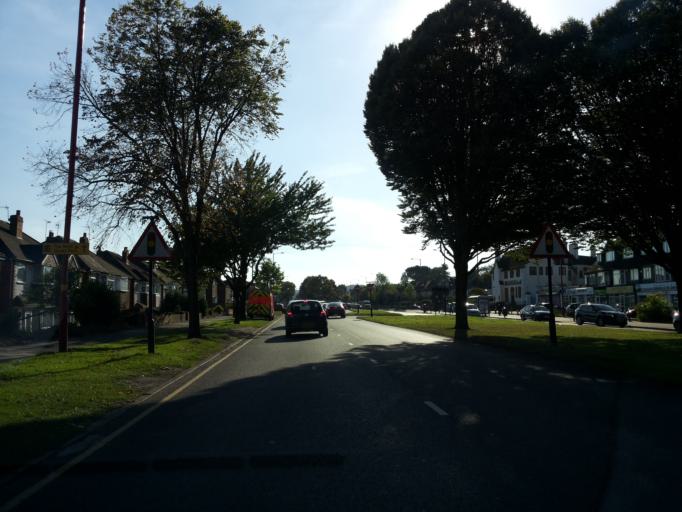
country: GB
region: England
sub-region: City and Borough of Birmingham
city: Bartley Green
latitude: 52.4031
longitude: -1.9806
